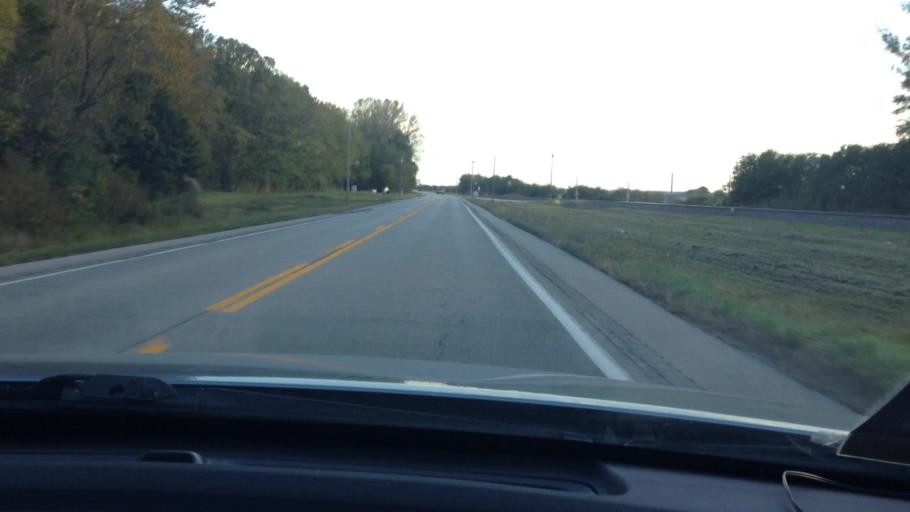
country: US
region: Kansas
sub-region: Leavenworth County
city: Leavenworth
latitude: 39.3049
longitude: -94.8481
